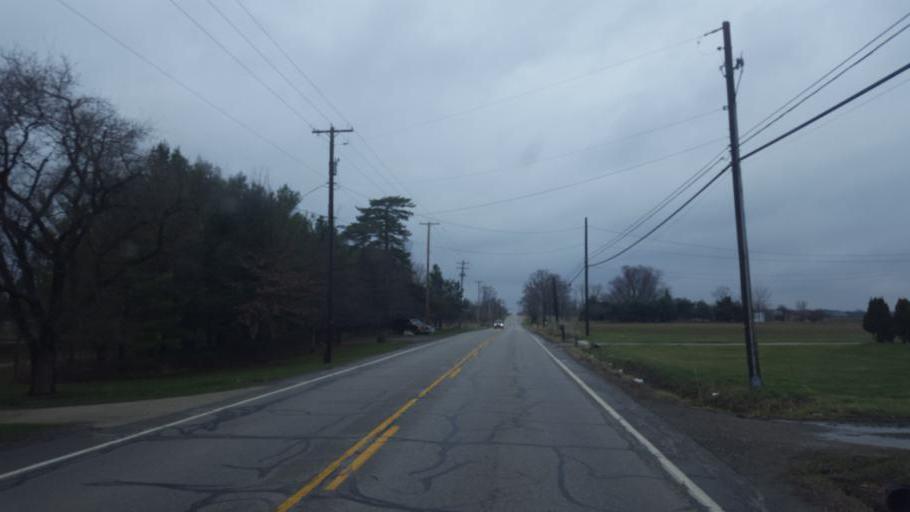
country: US
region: Ohio
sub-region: Medina County
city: Medina
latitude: 41.0941
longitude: -81.8642
